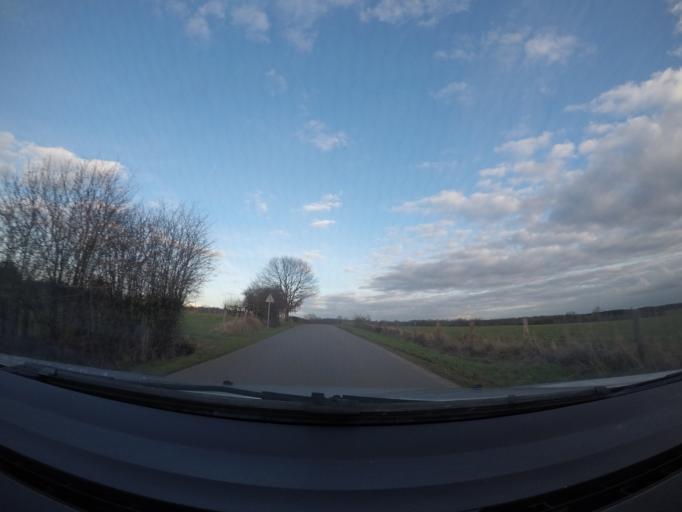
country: BE
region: Wallonia
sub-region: Province du Luxembourg
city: Tintigny
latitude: 49.7009
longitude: 5.5482
